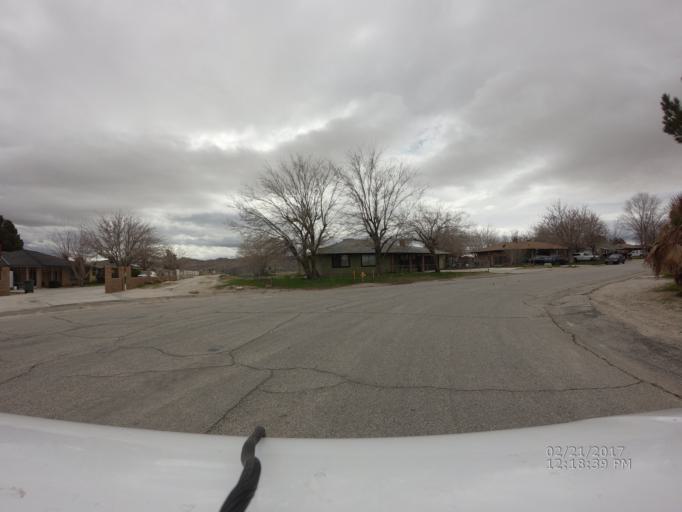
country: US
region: California
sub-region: Los Angeles County
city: Lake Los Angeles
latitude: 34.6327
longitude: -117.8557
